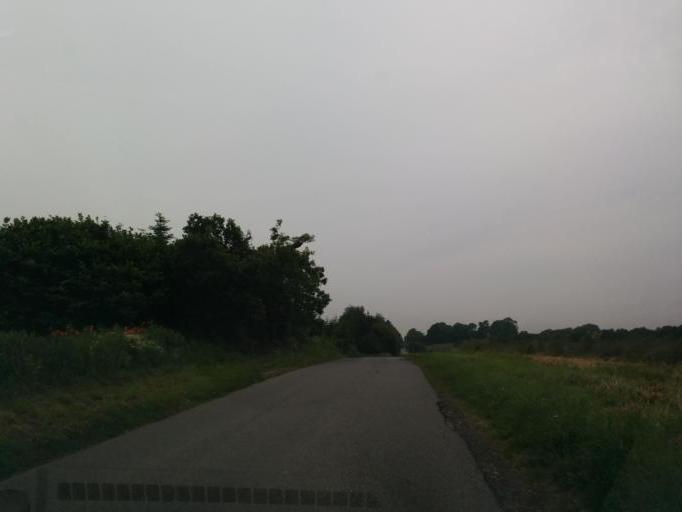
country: DK
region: Central Jutland
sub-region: Arhus Kommune
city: Logten
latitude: 56.2828
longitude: 10.3381
